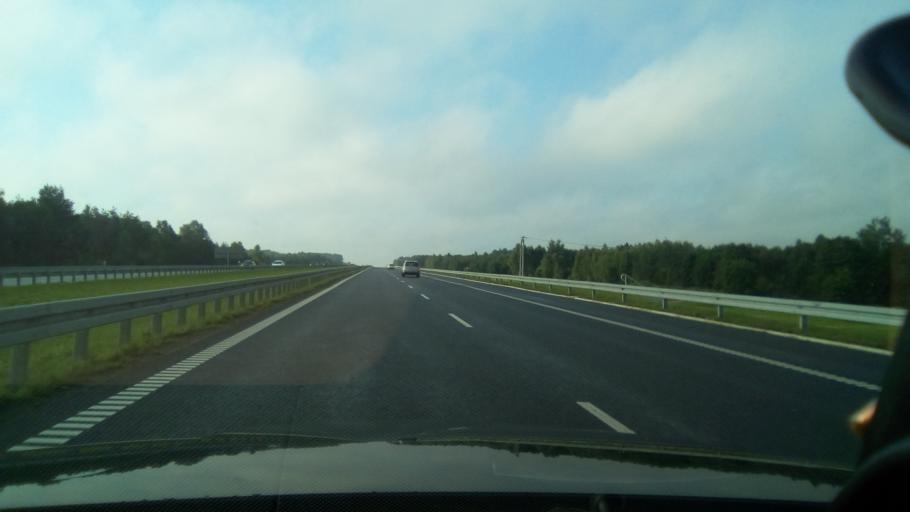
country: PL
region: Silesian Voivodeship
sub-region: Powiat czestochowski
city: Konopiska
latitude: 50.7255
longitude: 19.0577
